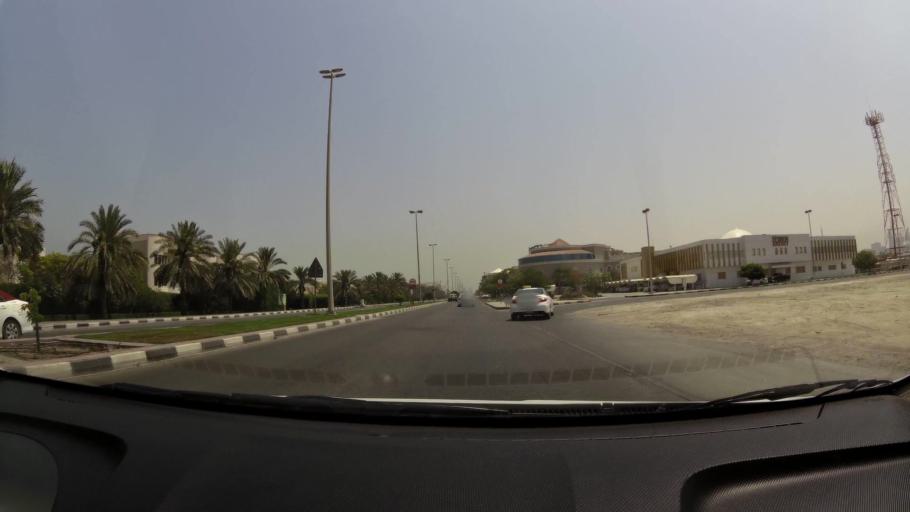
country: AE
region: Ash Shariqah
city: Sharjah
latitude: 25.3440
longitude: 55.3664
